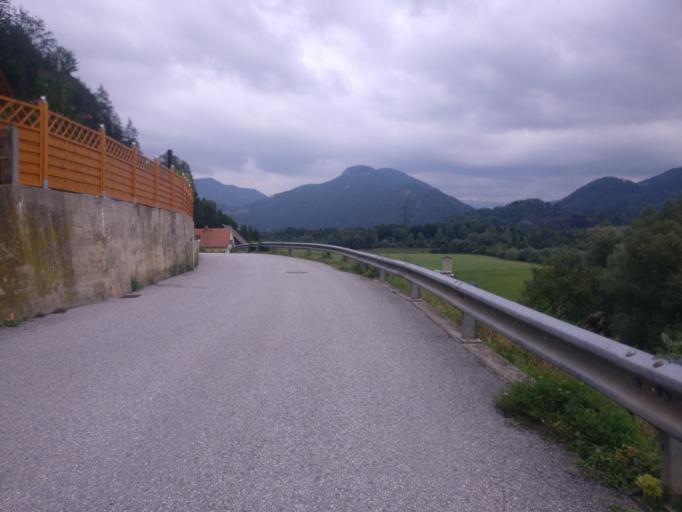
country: AT
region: Styria
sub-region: Politischer Bezirk Graz-Umgebung
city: Frohnleiten
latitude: 47.2537
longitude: 15.3107
